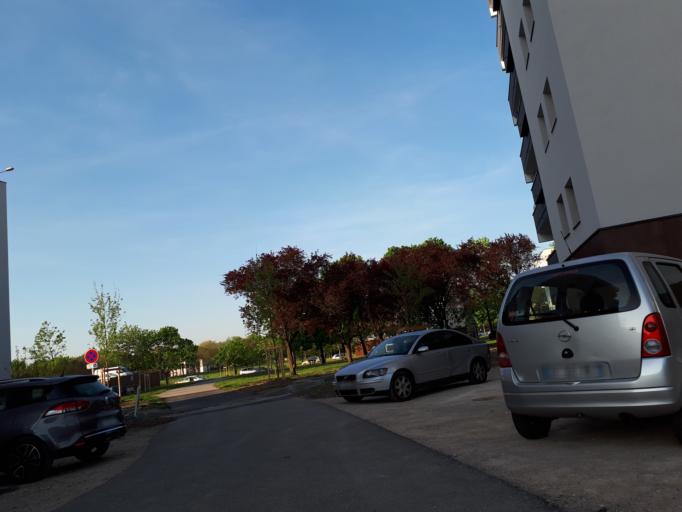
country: FR
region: Rhone-Alpes
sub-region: Departement de l'Isere
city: Bourgoin-Jallieu
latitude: 45.6115
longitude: 5.2717
